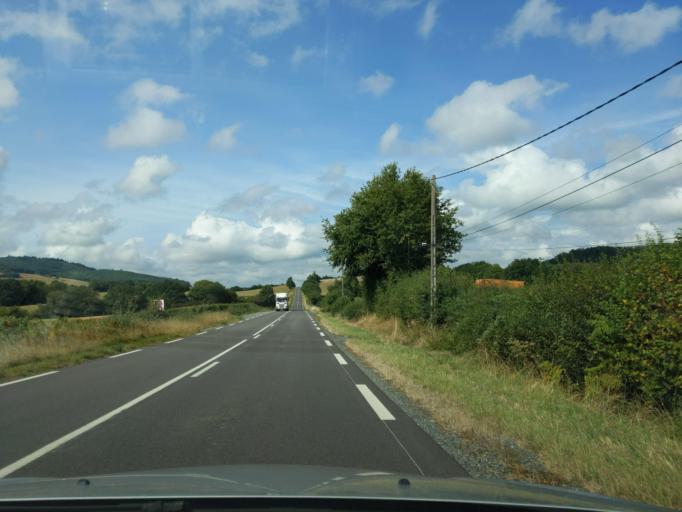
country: FR
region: Bourgogne
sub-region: Departement de Saone-et-Loire
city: Etang-sur-Arroux
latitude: 46.8490
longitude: 4.0741
